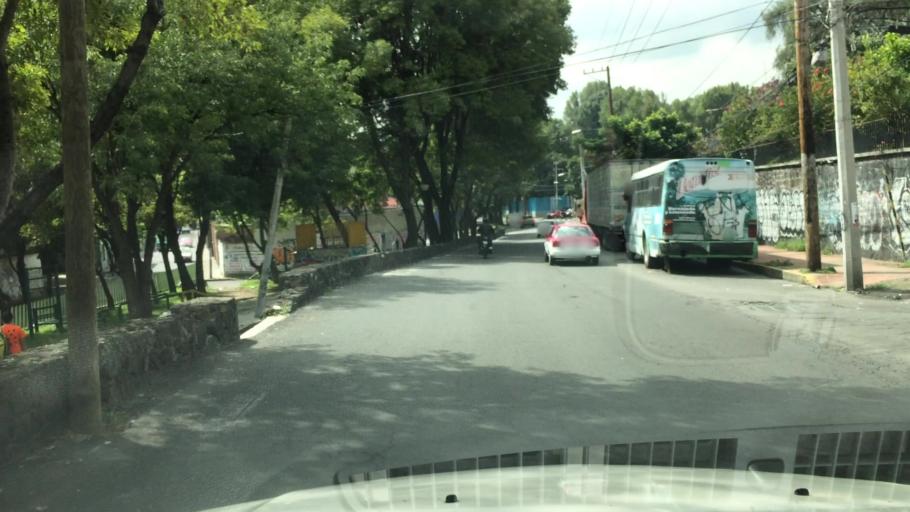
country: MX
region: Mexico City
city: Xochimilco
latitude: 19.2763
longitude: -99.1329
